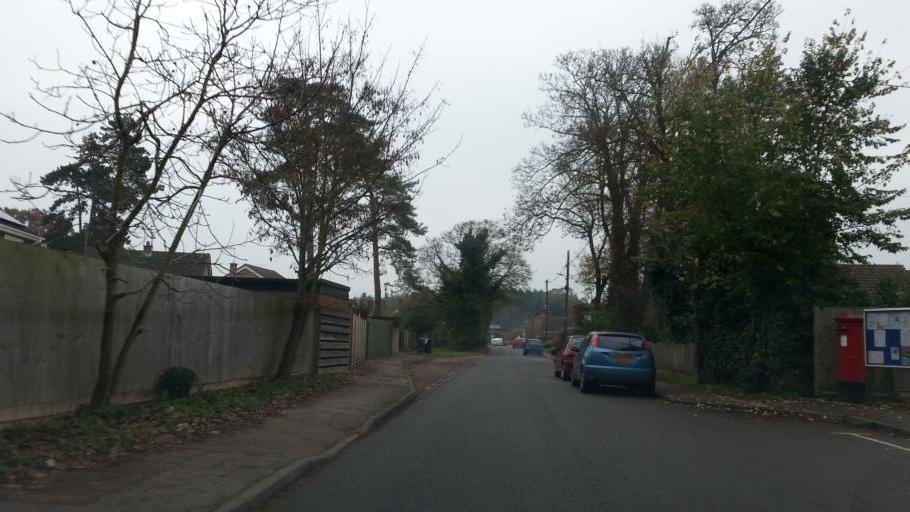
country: GB
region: England
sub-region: Suffolk
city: Thurston
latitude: 52.2521
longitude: 0.8064
